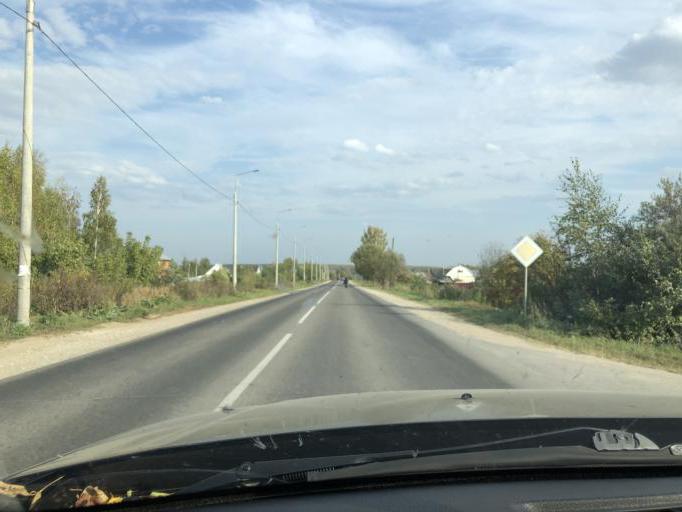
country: RU
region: Tula
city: Leninskiy
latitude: 54.2973
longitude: 37.4475
